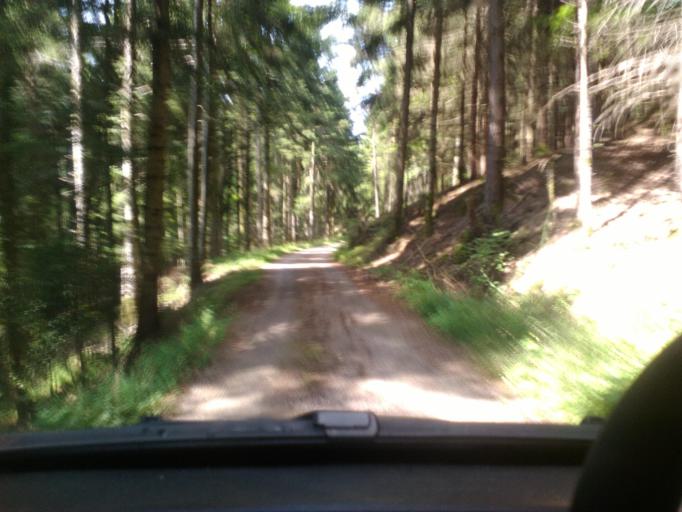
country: FR
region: Lorraine
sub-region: Departement des Vosges
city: Sainte-Marguerite
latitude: 48.2976
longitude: 6.9942
